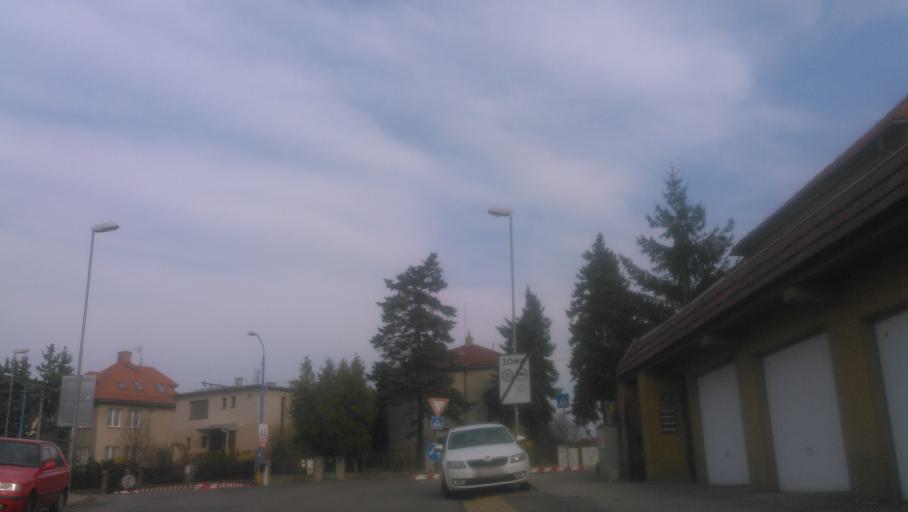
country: SK
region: Bratislavsky
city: Bratislava
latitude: 48.1483
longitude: 17.0887
